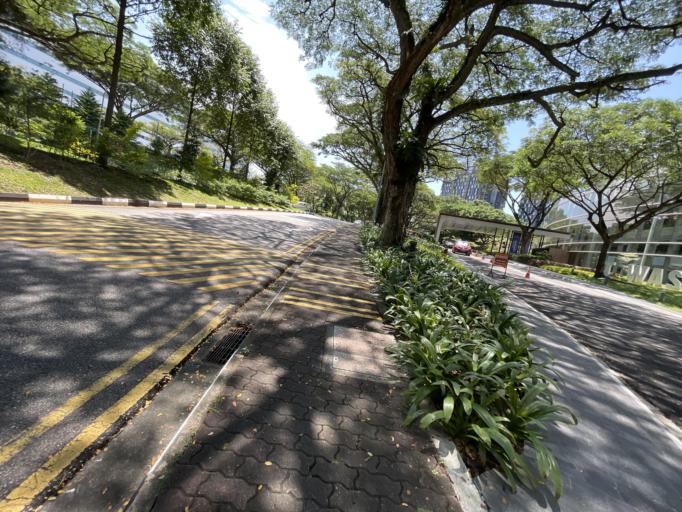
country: SG
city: Singapore
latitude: 1.3012
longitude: 103.7723
